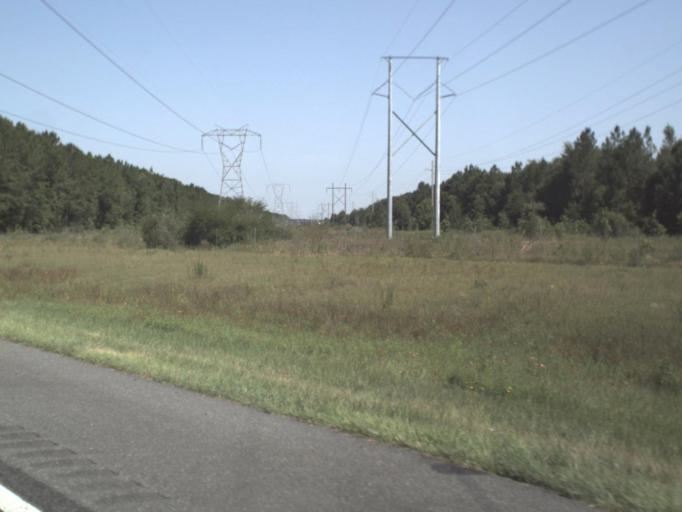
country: US
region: Florida
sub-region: Suwannee County
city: Live Oak
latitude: 30.3525
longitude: -83.1655
